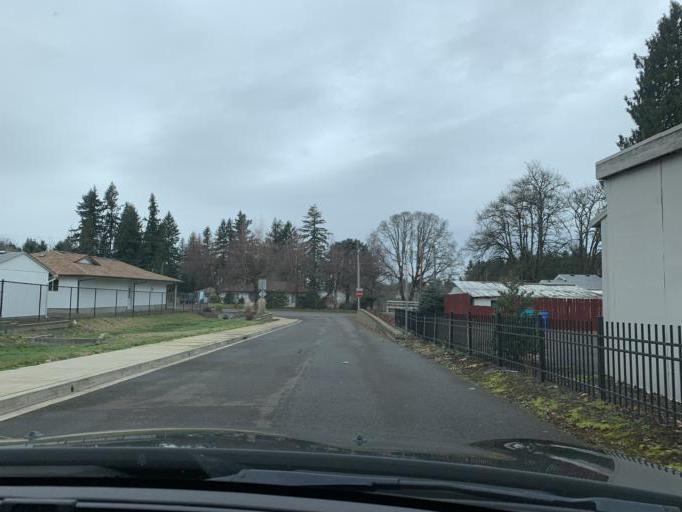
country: US
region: Washington
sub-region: Clark County
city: Five Corners
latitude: 45.6854
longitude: -122.5844
